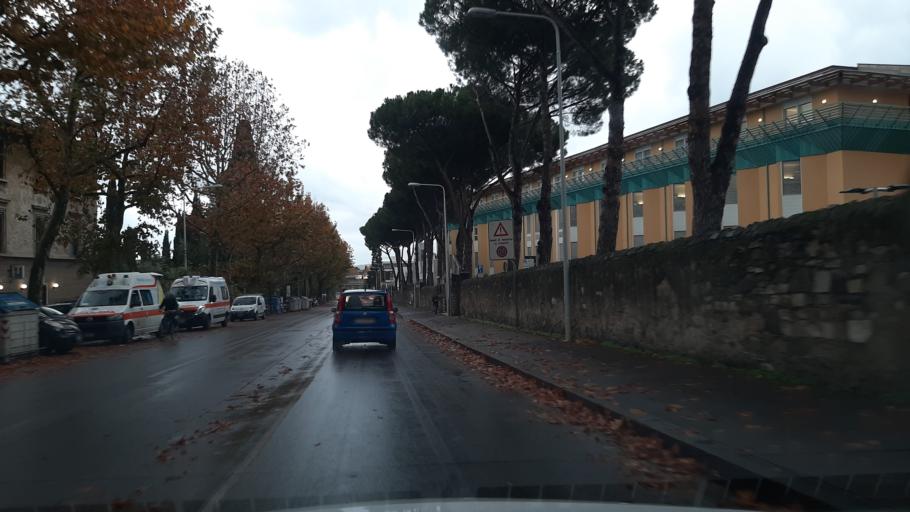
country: IT
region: Tuscany
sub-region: Province of Florence
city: Florence
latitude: 43.8065
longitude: 11.2495
